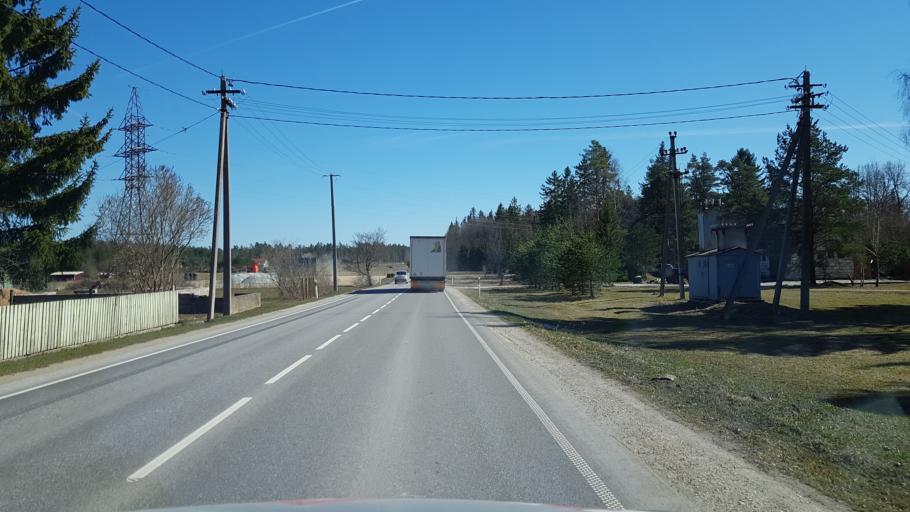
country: EE
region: Laeaene-Virumaa
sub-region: Rakvere linn
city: Rakvere
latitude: 59.3358
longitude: 26.3930
